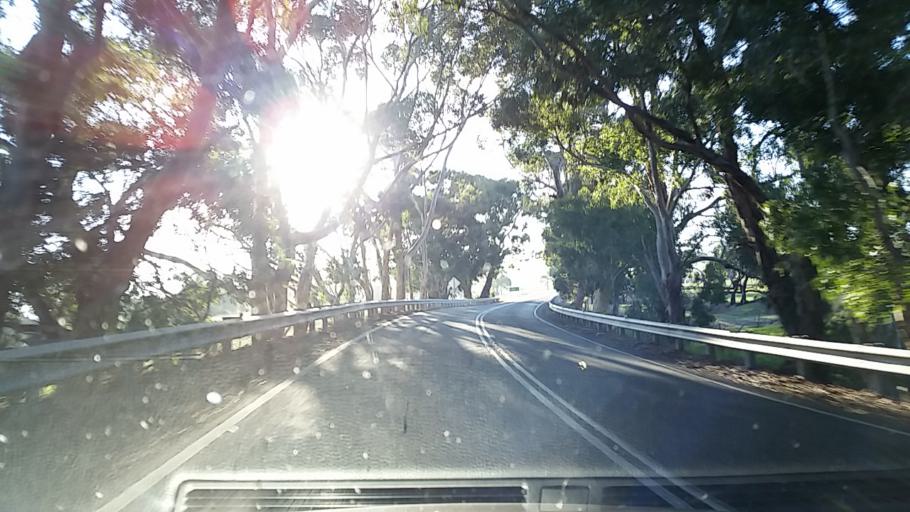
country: AU
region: South Australia
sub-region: Alexandrina
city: Goolwa
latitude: -35.3938
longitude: 138.7627
